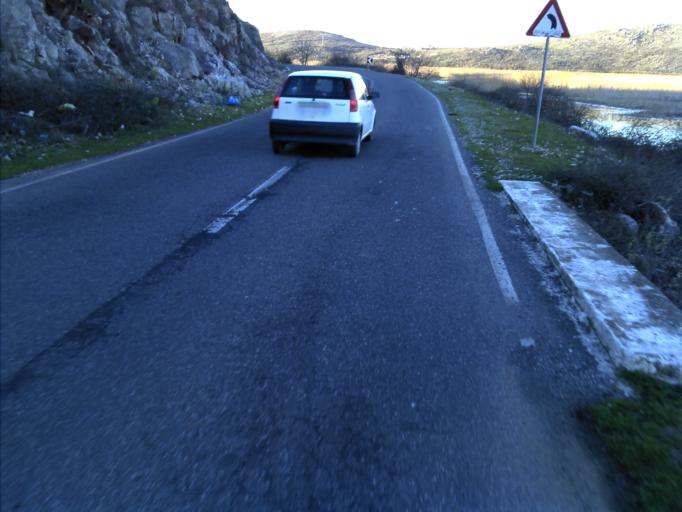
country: AL
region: Shkoder
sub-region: Rrethi i Shkodres
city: Velipoje
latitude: 41.9270
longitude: 19.4387
